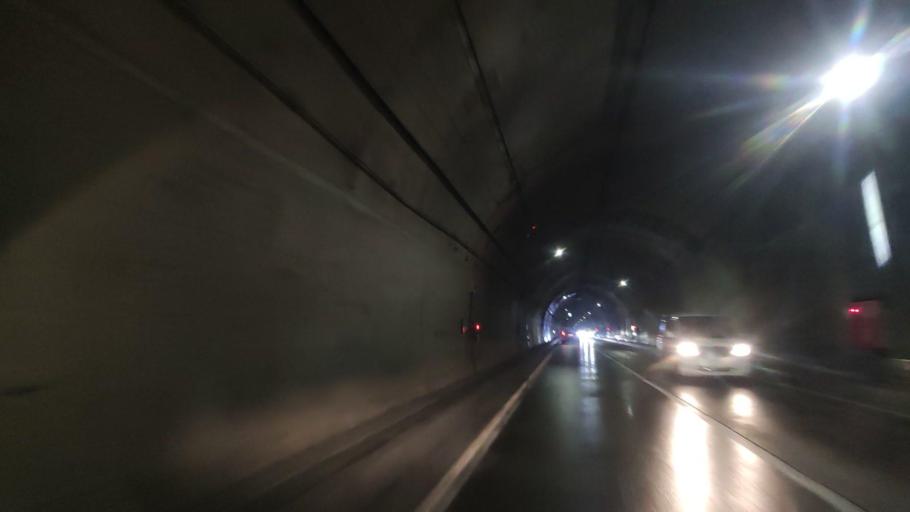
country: JP
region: Hokkaido
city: Rumoi
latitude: 43.7284
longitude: 141.3338
